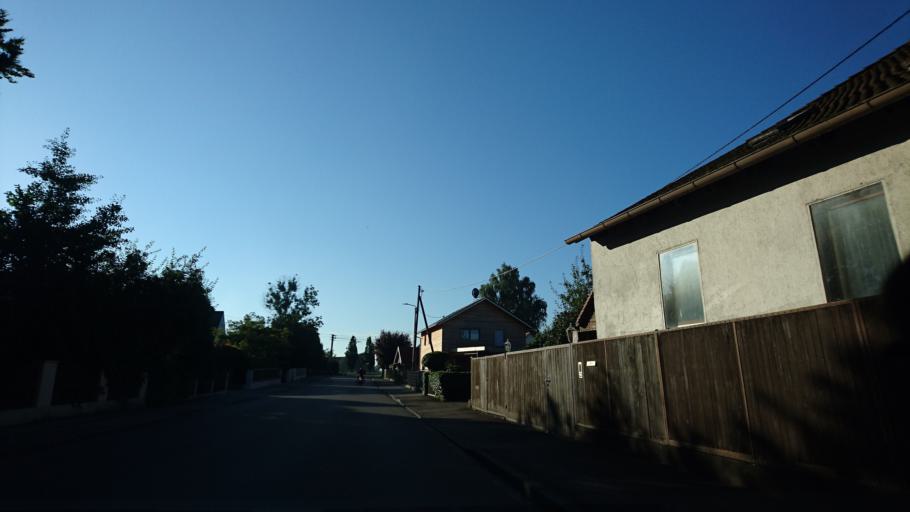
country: DE
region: Bavaria
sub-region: Swabia
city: Grossaitingen
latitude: 48.2286
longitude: 10.7841
